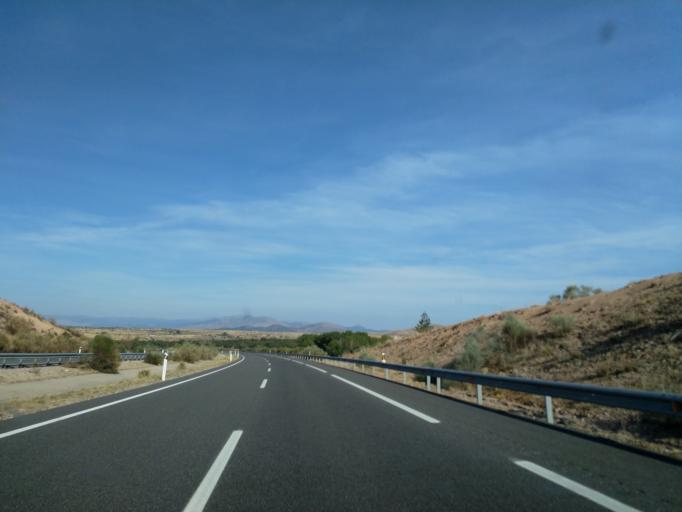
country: ES
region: Castille and Leon
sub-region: Provincia de Segovia
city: Villacastin
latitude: 40.7510
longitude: -4.4610
